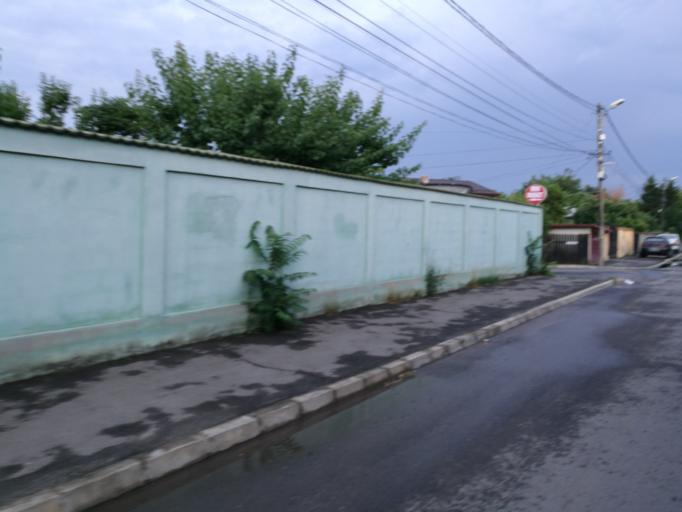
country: RO
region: Ilfov
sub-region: Comuna Mogosoaia
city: Mogosoaia
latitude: 44.5248
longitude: 26.0059
